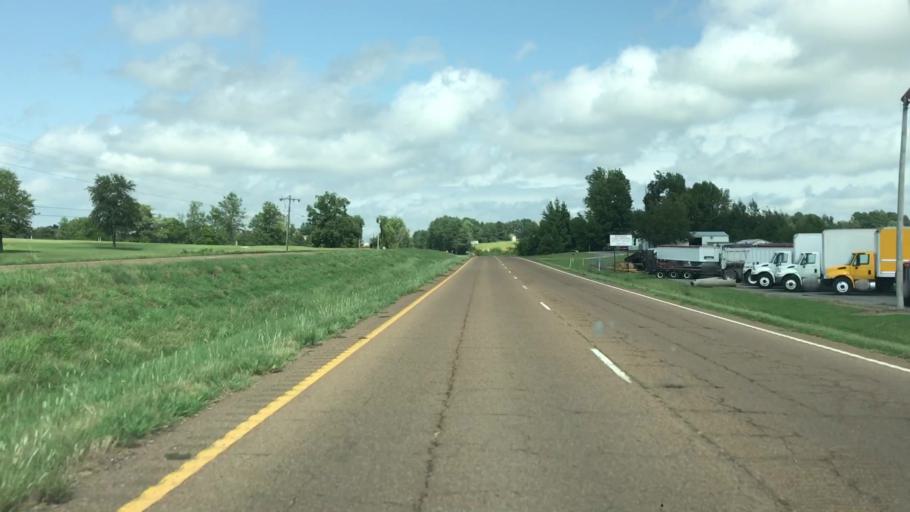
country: US
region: Tennessee
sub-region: Obion County
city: Englewood
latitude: 36.3521
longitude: -89.1424
